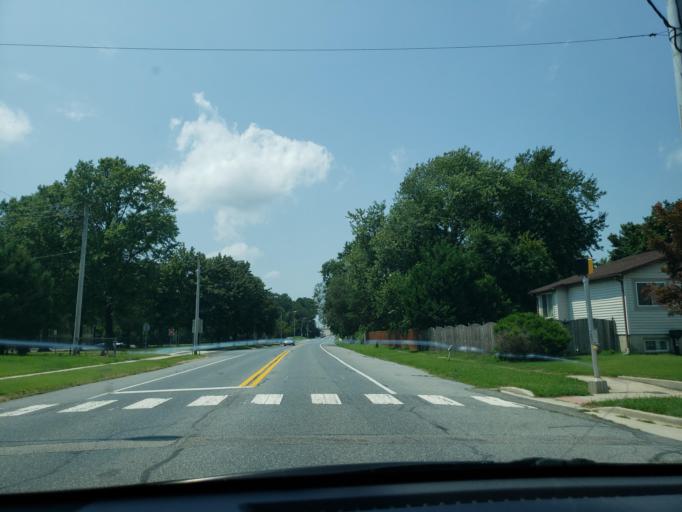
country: US
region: Delaware
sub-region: Kent County
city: Rodney Village
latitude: 39.1327
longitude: -75.5371
